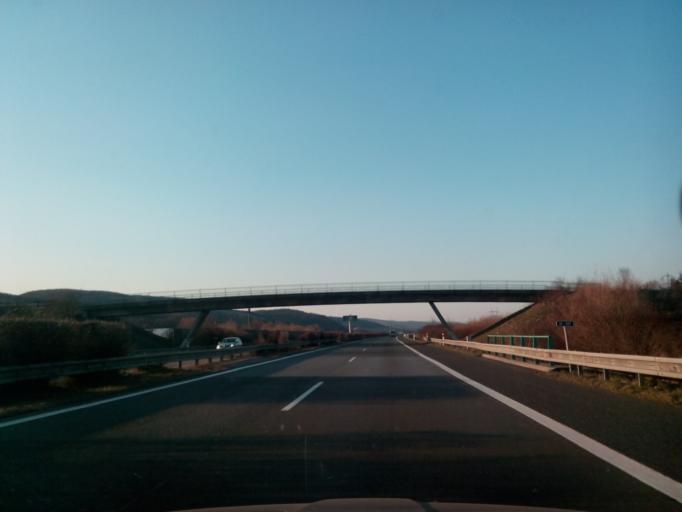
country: SK
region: Presovsky
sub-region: Okres Presov
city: Presov
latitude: 48.8770
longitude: 21.2523
